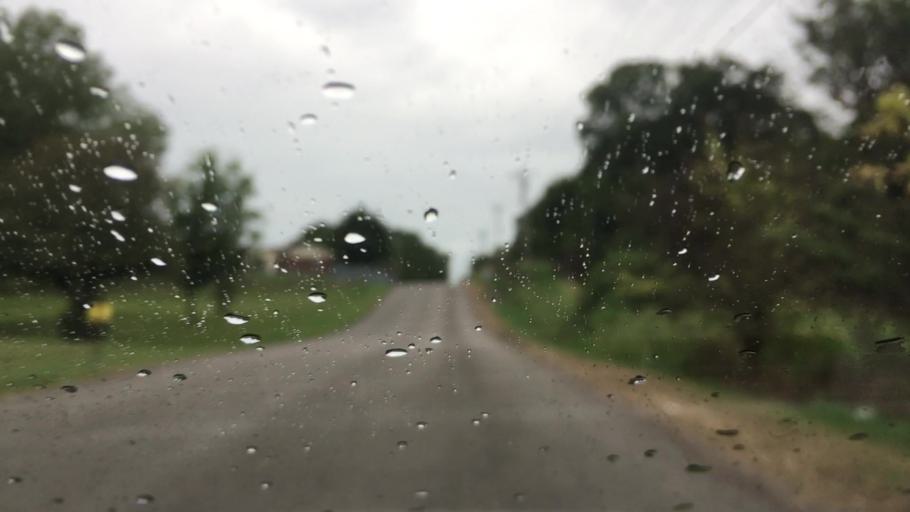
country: US
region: Oklahoma
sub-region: Cherokee County
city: Tahlequah
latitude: 35.9298
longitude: -95.1300
